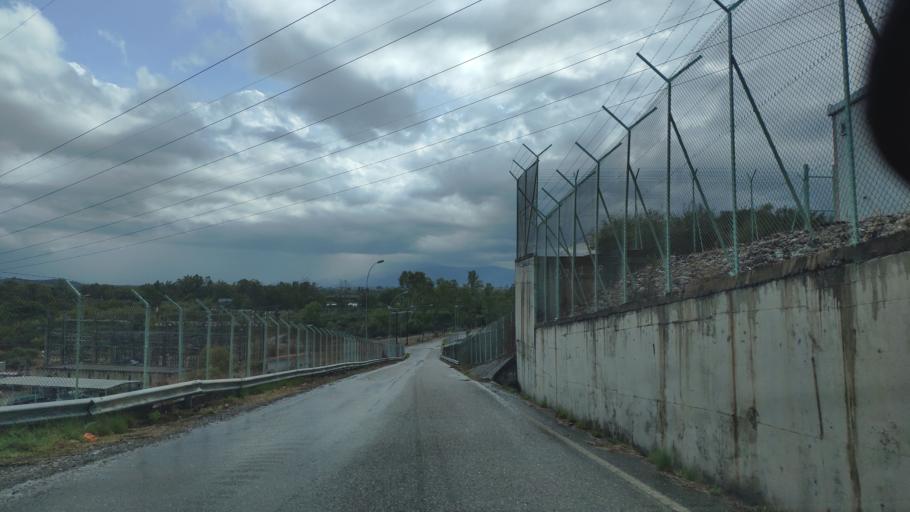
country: GR
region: West Greece
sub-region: Nomos Aitolias kai Akarnanias
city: Neapolis
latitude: 38.6765
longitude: 21.3245
